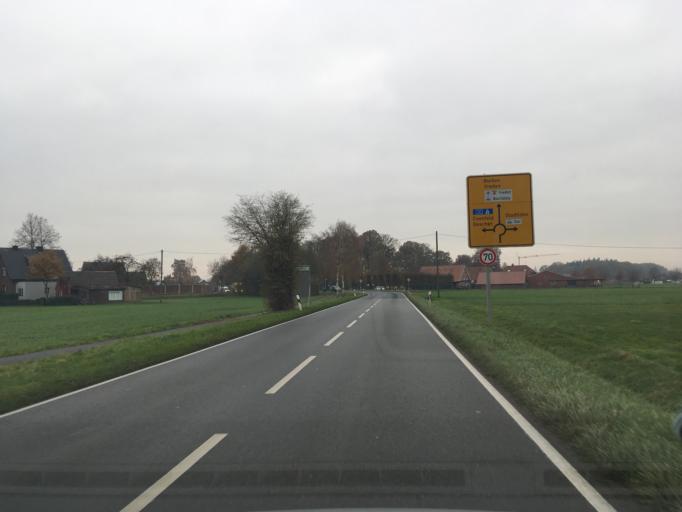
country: DE
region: North Rhine-Westphalia
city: Stadtlohn
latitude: 51.9857
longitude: 6.9473
